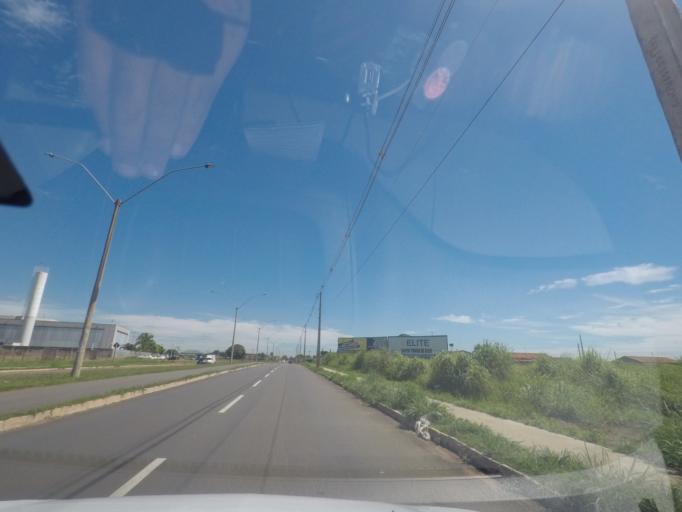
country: BR
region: Goias
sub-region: Aparecida De Goiania
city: Aparecida de Goiania
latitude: -16.7907
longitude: -49.3298
